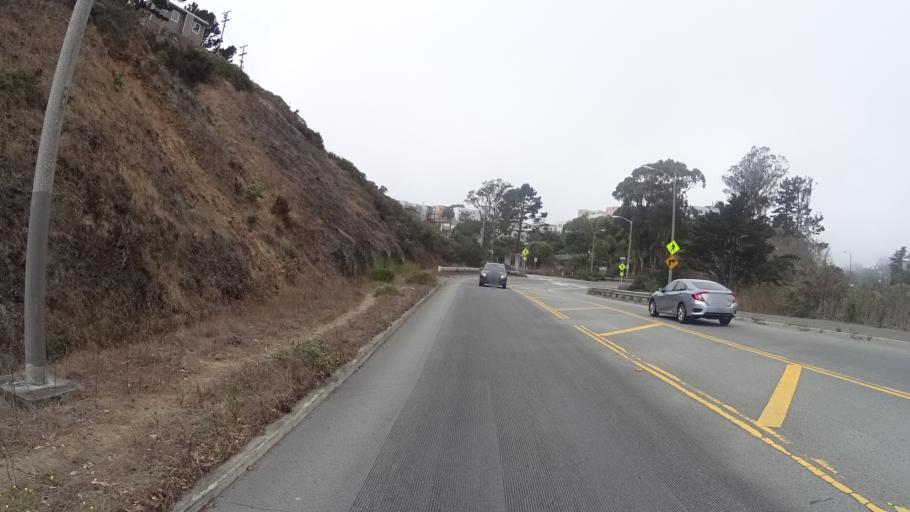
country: US
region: California
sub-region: San Mateo County
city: Daly City
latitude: 37.7409
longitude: -122.4450
